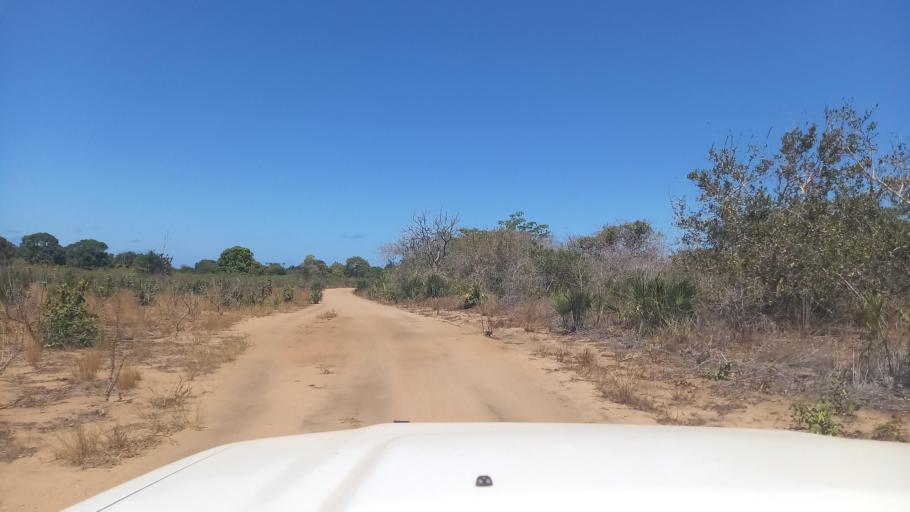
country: MZ
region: Cabo Delgado
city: Pemba
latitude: -13.4223
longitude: 40.5130
